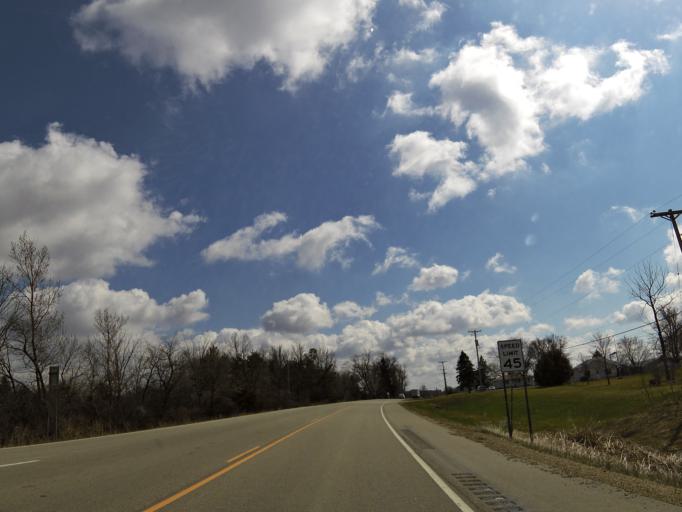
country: US
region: Minnesota
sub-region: Dodge County
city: Dodge Center
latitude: 44.1602
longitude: -92.8996
